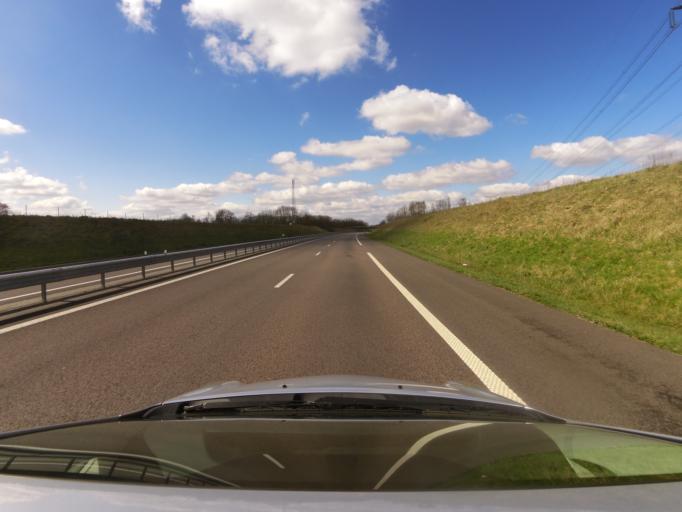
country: FR
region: Haute-Normandie
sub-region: Departement de la Seine-Maritime
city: Cleres
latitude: 49.6310
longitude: 1.1253
